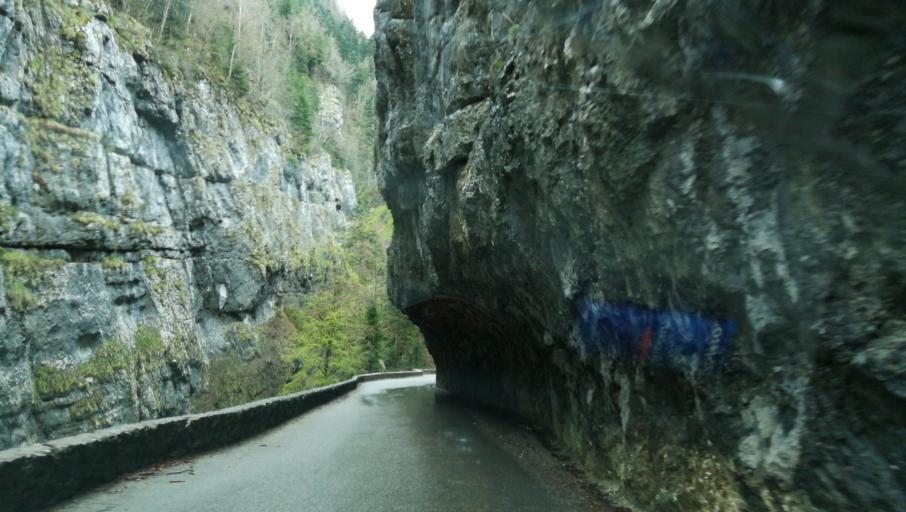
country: FR
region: Rhone-Alpes
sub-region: Departement de l'Isere
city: Villard-de-Lans
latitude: 45.0745
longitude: 5.5202
